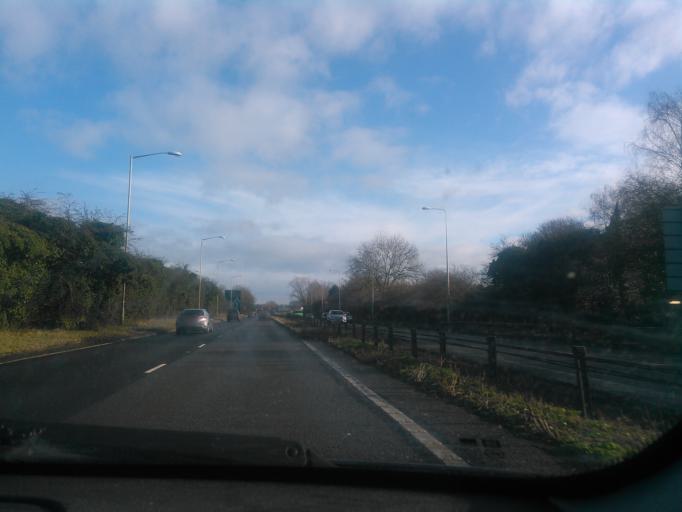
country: GB
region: England
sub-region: Staffordshire
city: Uttoxeter
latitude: 52.9095
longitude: -1.8795
